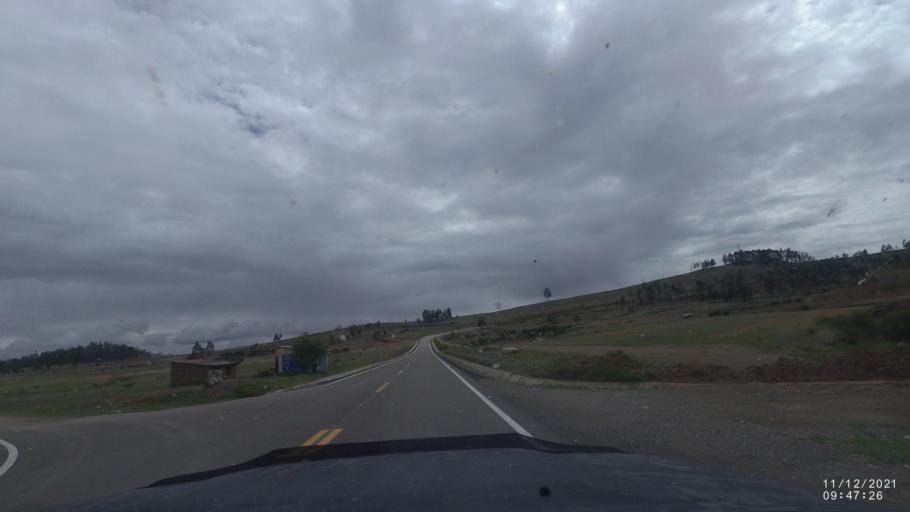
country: BO
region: Cochabamba
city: Tarata
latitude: -17.7858
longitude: -65.9626
